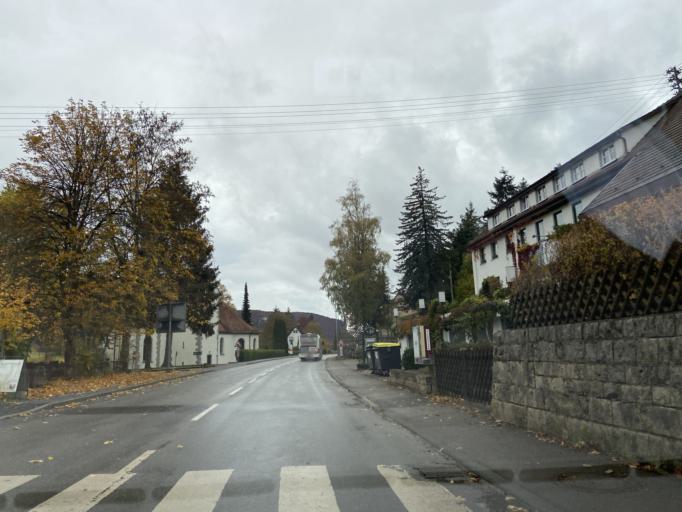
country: DE
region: Baden-Wuerttemberg
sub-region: Tuebingen Region
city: Schwenningen
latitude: 48.0840
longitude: 9.0380
